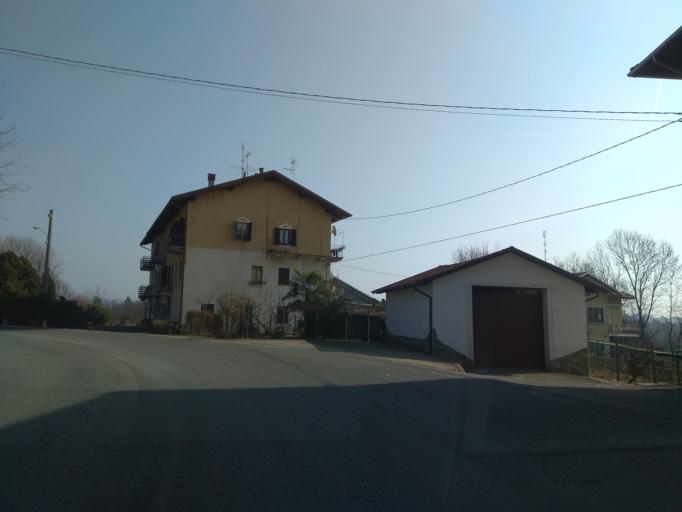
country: IT
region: Piedmont
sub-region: Provincia di Biella
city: Mosso
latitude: 45.6487
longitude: 8.1453
